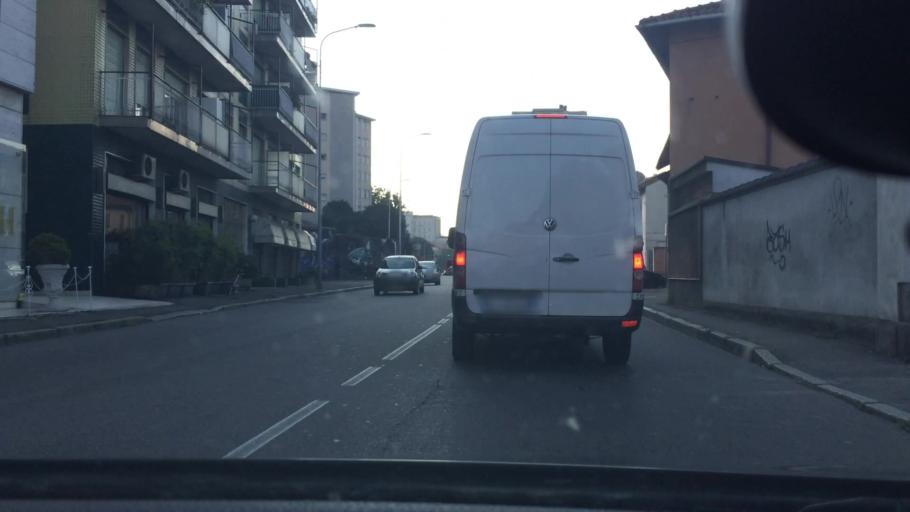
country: IT
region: Lombardy
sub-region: Citta metropolitana di Milano
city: Rho
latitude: 45.5298
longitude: 9.0460
